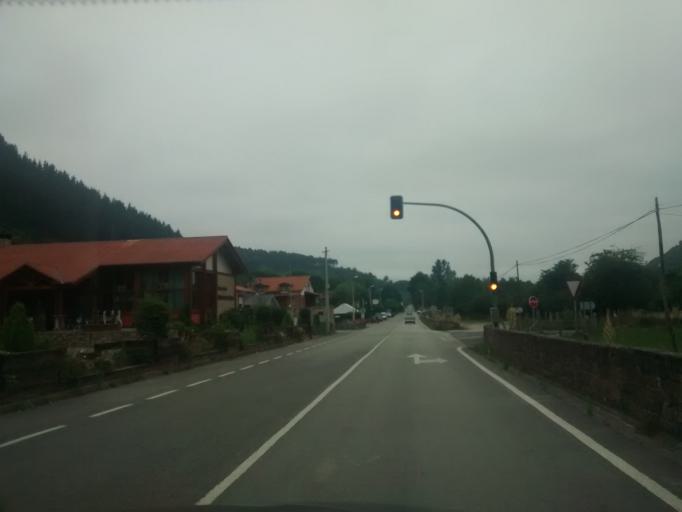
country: ES
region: Cantabria
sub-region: Provincia de Cantabria
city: Ruente
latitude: 43.2006
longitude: -4.3051
